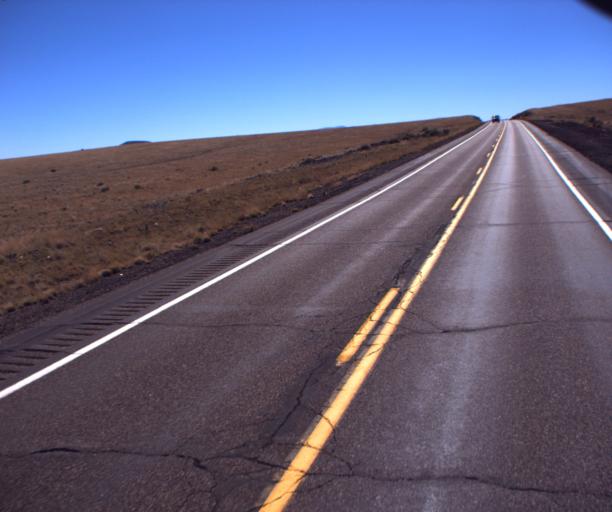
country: US
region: Arizona
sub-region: Apache County
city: Springerville
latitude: 34.3033
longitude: -109.3776
